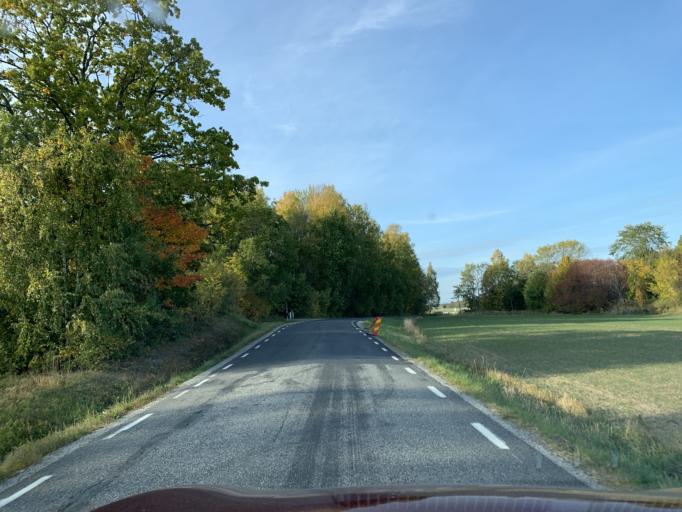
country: SE
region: Stockholm
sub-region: Upplands-Bro Kommun
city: Bro
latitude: 59.5032
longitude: 17.5867
